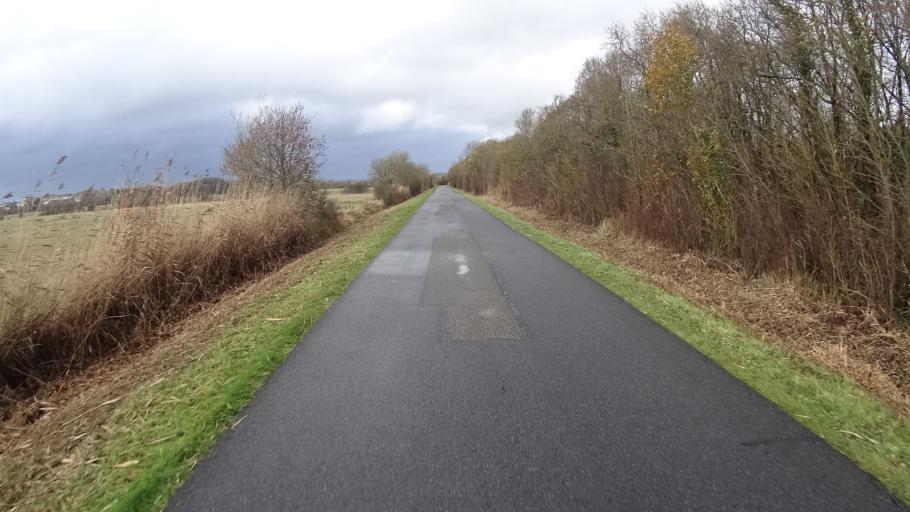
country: FR
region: Brittany
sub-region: Departement du Morbihan
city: Rieux
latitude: 47.5921
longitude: -2.0874
